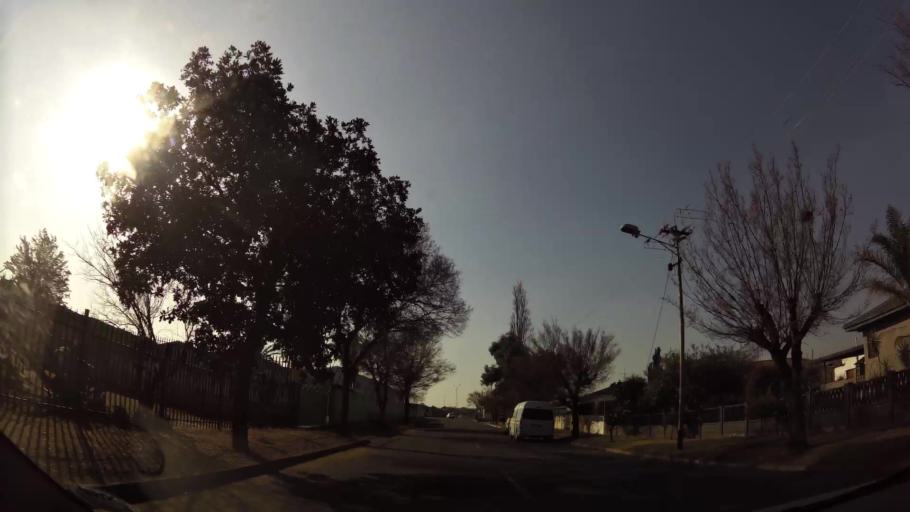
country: ZA
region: Gauteng
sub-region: West Rand District Municipality
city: Randfontein
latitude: -26.1757
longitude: 27.7065
